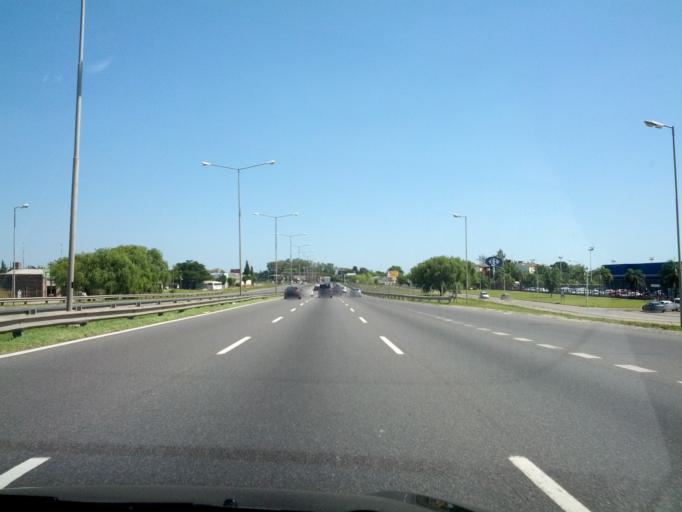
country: AR
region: Buenos Aires
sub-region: Partido de Campana
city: Campana
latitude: -34.1884
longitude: -58.9457
